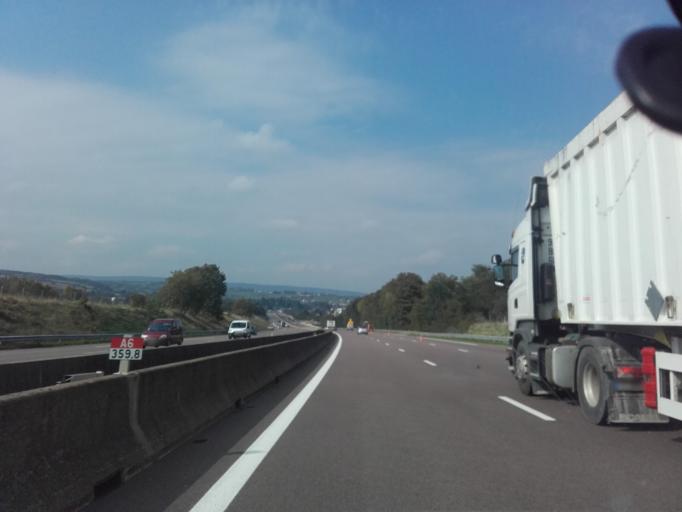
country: FR
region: Bourgogne
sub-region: Departement de Saone-et-Loire
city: Tournus
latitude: 46.5462
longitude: 4.9152
